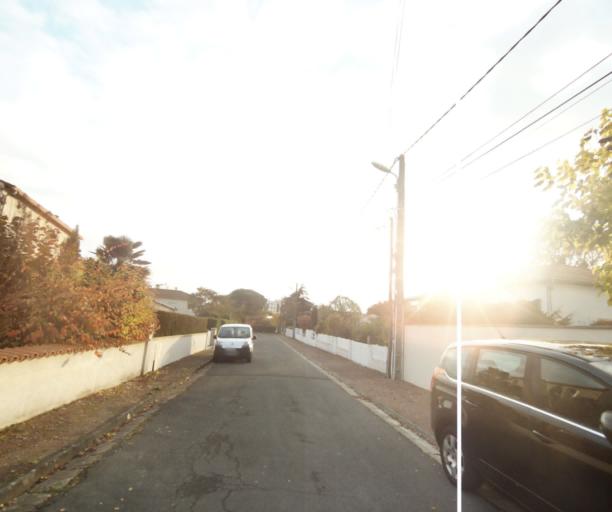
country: FR
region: Poitou-Charentes
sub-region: Departement de la Charente-Maritime
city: Saintes
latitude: 45.7518
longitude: -0.6465
